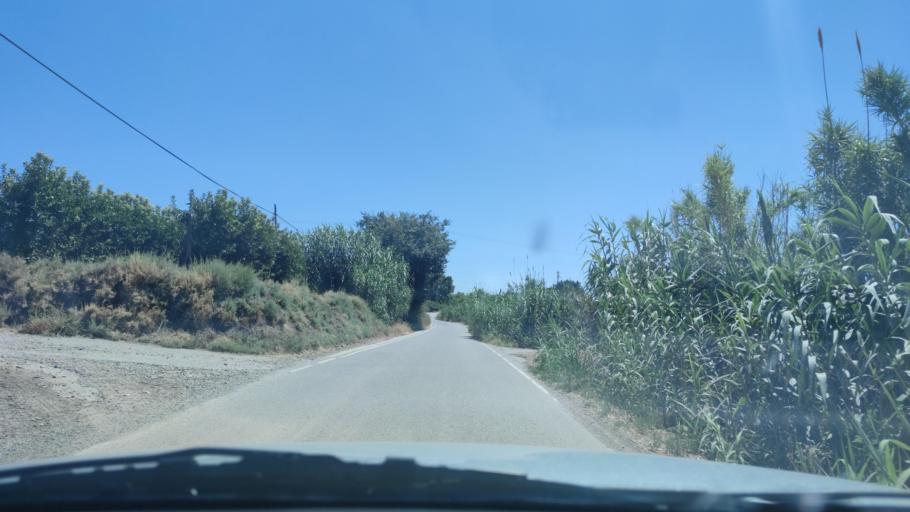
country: ES
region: Catalonia
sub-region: Provincia de Lleida
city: Lleida
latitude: 41.6344
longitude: 0.6564
